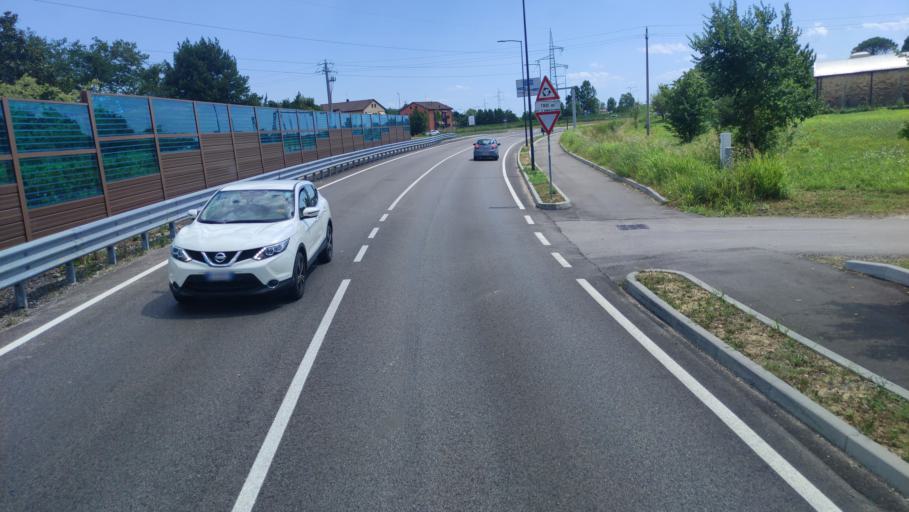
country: IT
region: Veneto
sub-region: Provincia di Venezia
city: Scorze
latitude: 45.5690
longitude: 12.1018
